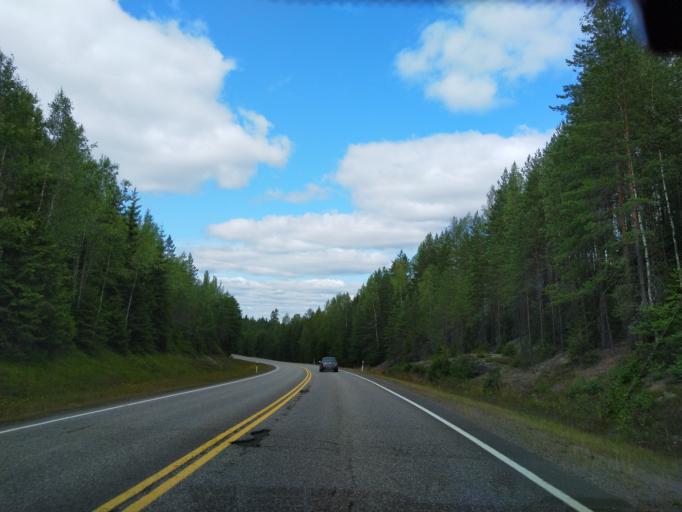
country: FI
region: Haeme
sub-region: Riihimaeki
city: Loppi
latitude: 60.7416
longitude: 24.3619
